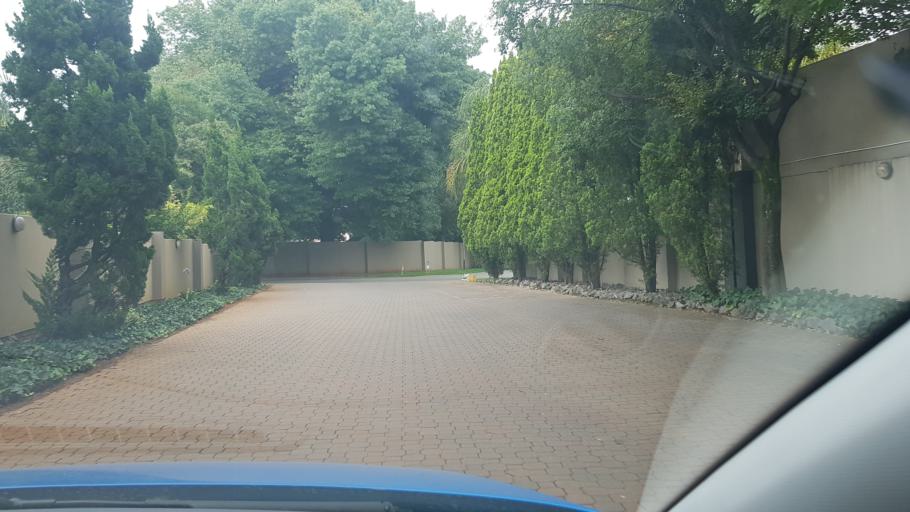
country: ZA
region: Gauteng
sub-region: Ekurhuleni Metropolitan Municipality
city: Germiston
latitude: -26.1670
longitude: 28.1576
